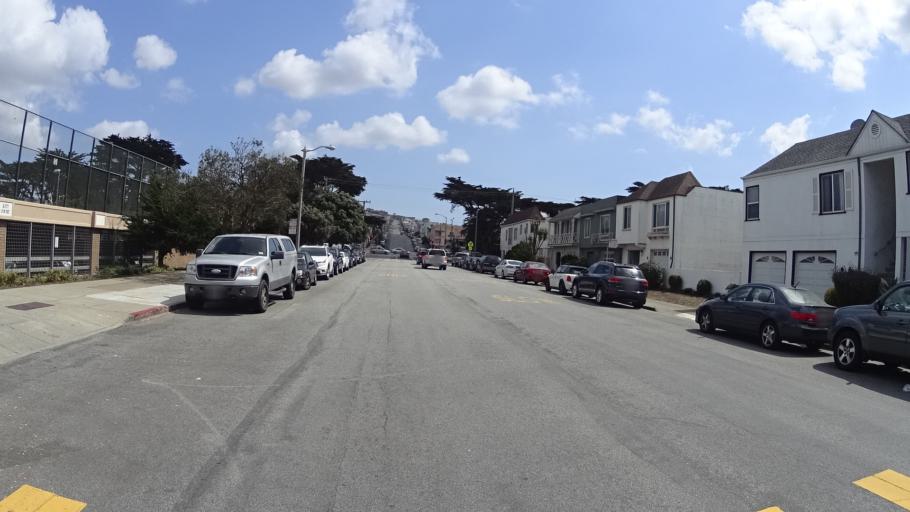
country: US
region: California
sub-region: San Mateo County
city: Daly City
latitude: 37.7459
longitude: -122.4962
